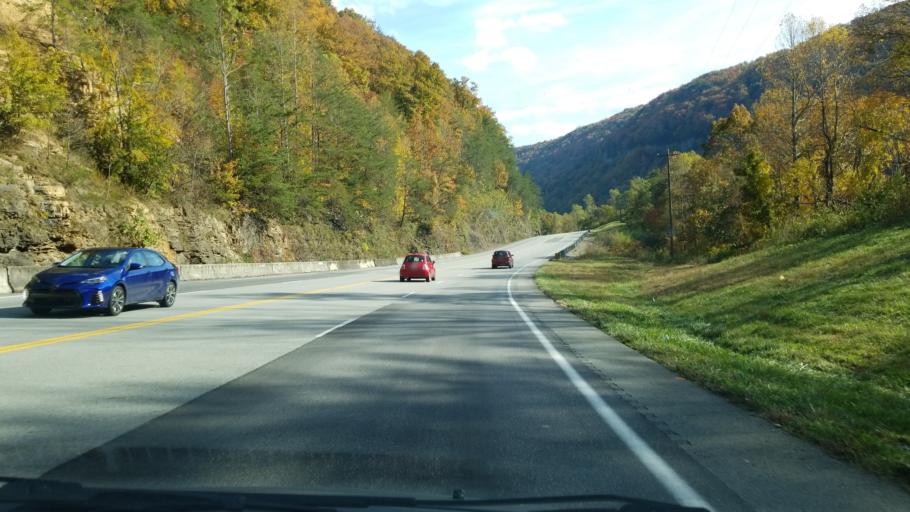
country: US
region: Tennessee
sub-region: Sequatchie County
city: Dunlap
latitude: 35.4160
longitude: -85.4136
